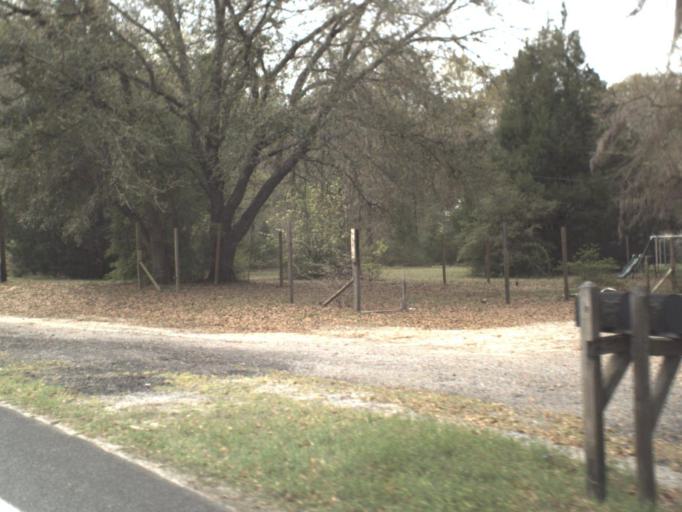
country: US
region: Florida
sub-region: Calhoun County
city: Blountstown
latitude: 30.5615
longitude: -85.1841
